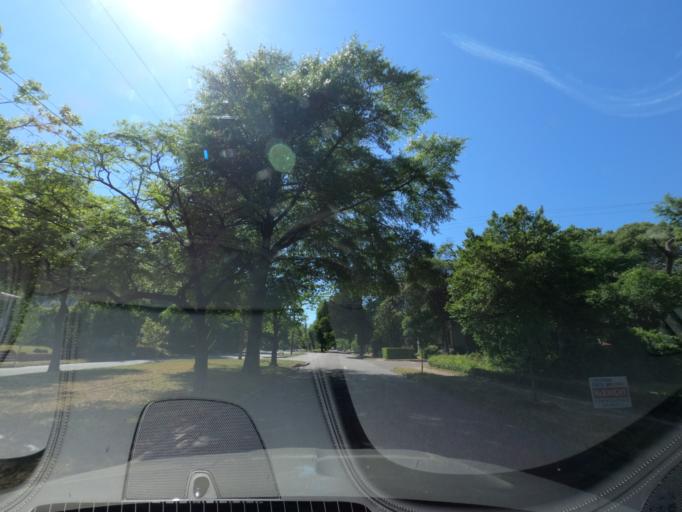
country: US
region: Georgia
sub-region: Richmond County
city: Augusta
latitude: 33.4705
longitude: -82.0171
